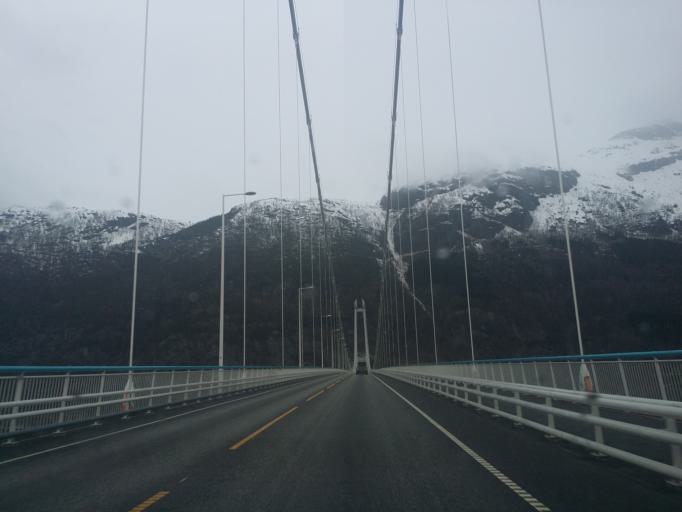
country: NO
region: Hordaland
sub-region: Ulvik
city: Ulvik
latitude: 60.4750
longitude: 6.8346
